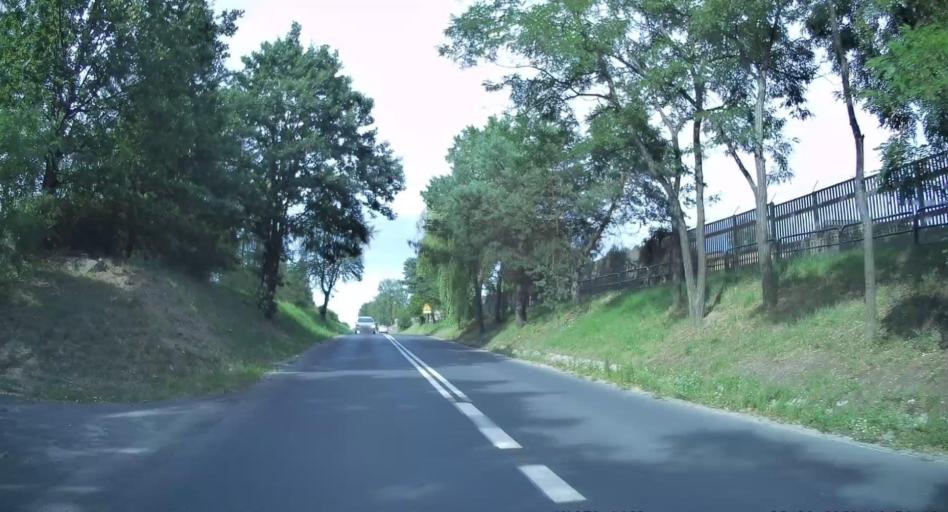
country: PL
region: Lodz Voivodeship
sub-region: Powiat tomaszowski
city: Tomaszow Mazowiecki
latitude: 51.5159
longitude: 20.0013
